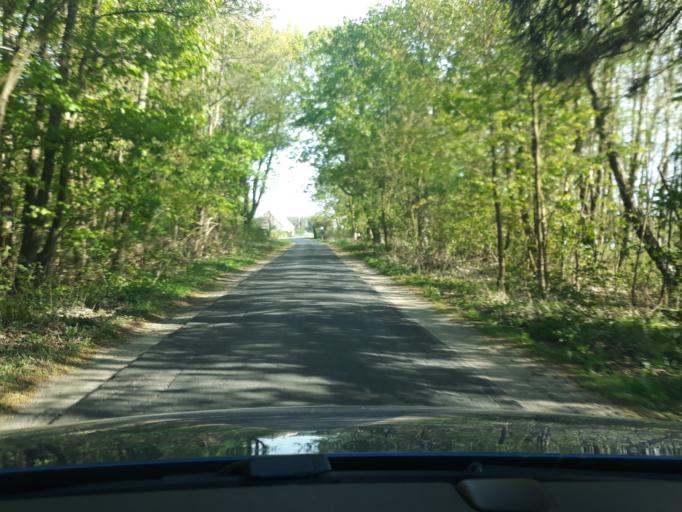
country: PL
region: Pomeranian Voivodeship
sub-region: Powiat czluchowski
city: Przechlewo
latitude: 53.8753
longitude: 17.3296
